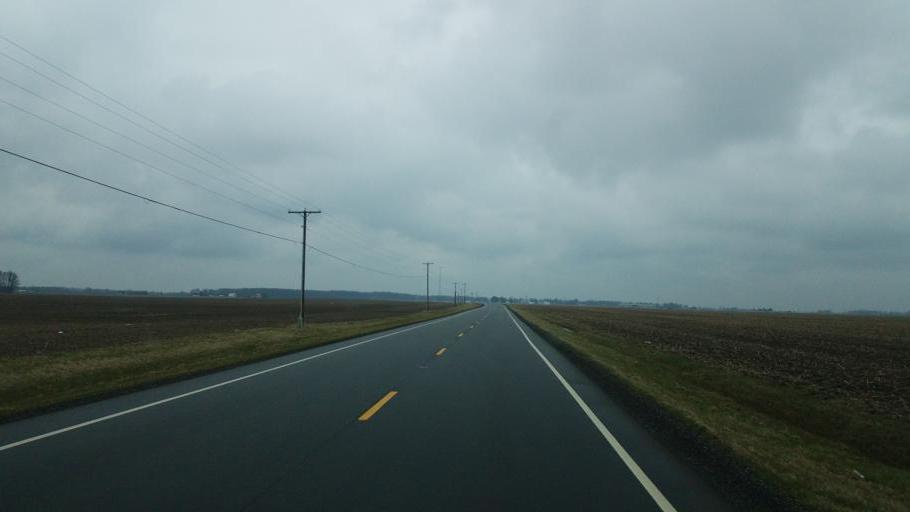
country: US
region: Ohio
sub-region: Delaware County
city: Ashley
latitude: 40.4380
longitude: -82.9523
